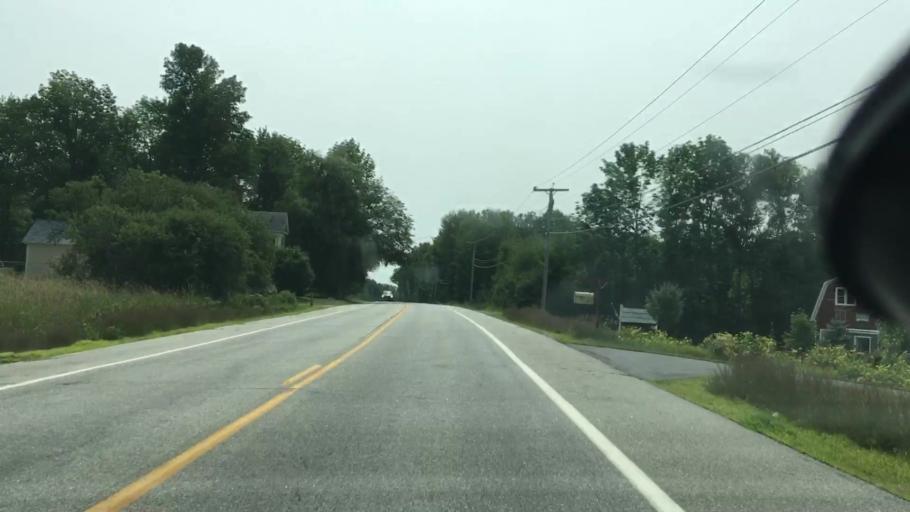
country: US
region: Maine
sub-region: Androscoggin County
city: Livermore Falls
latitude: 44.4293
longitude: -70.1463
